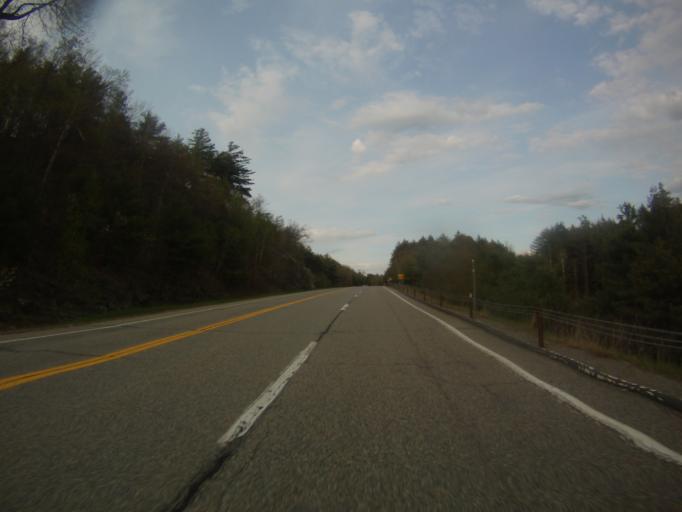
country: US
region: New York
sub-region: Essex County
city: Ticonderoga
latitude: 43.7435
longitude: -73.5839
